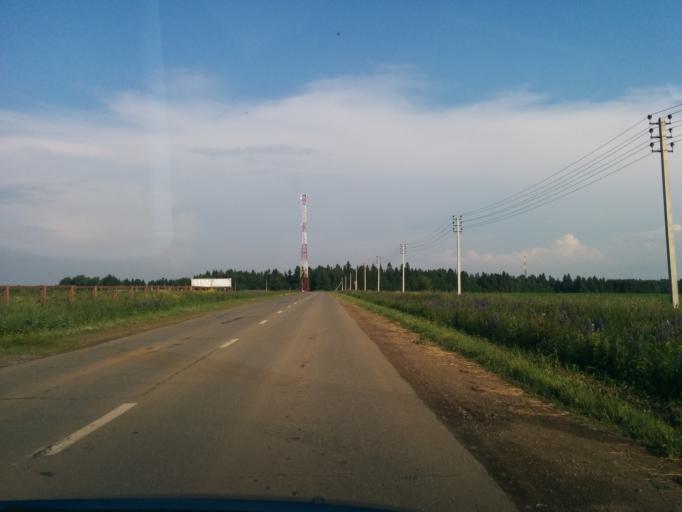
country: RU
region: Perm
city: Polazna
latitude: 58.2391
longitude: 56.2735
